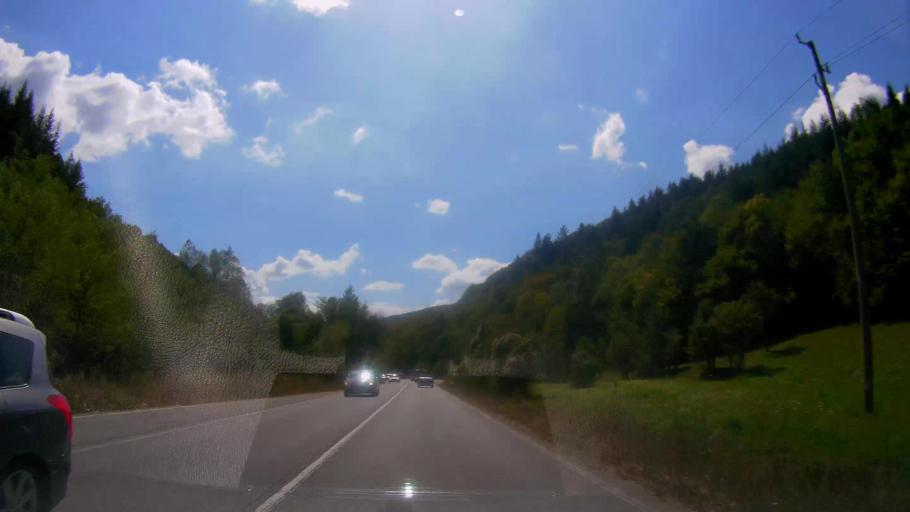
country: BG
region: Stara Zagora
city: Gurkovo
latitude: 42.7474
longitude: 25.7094
